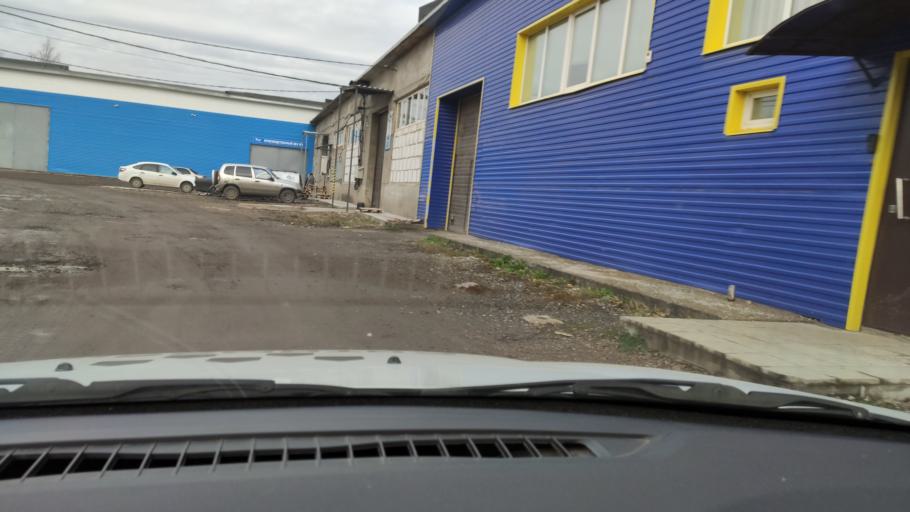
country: RU
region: Perm
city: Perm
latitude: 57.9584
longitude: 56.2163
